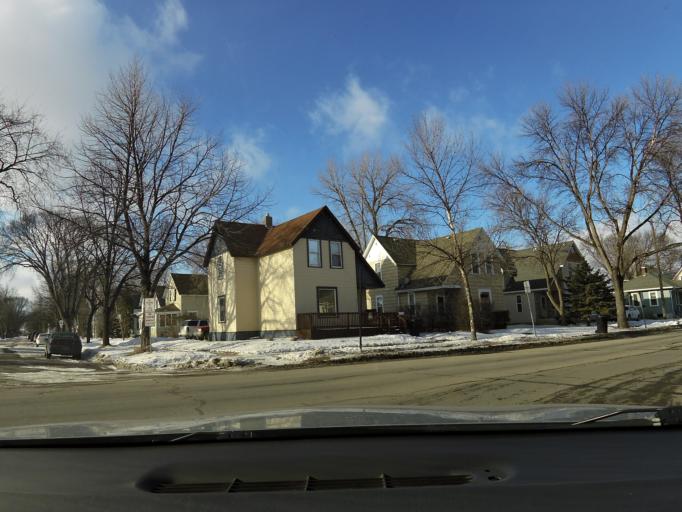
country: US
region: North Dakota
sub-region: Grand Forks County
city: Grand Forks
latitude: 47.9241
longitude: -97.0380
